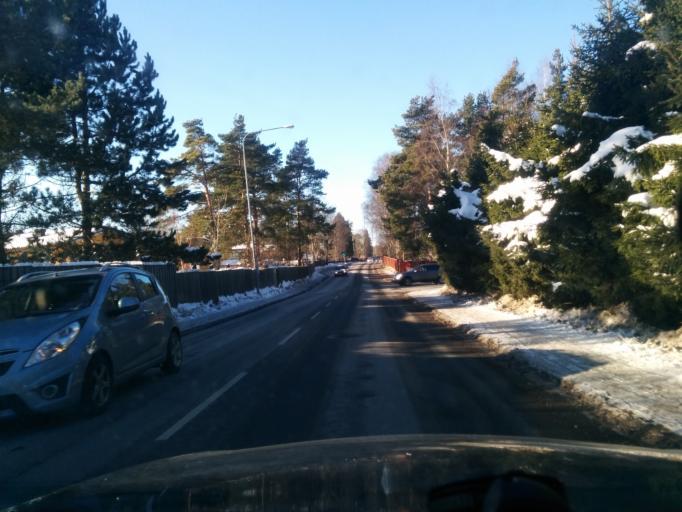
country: SE
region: Stockholm
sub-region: Vallentuna Kommun
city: Vallentuna
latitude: 59.4976
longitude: 18.0708
